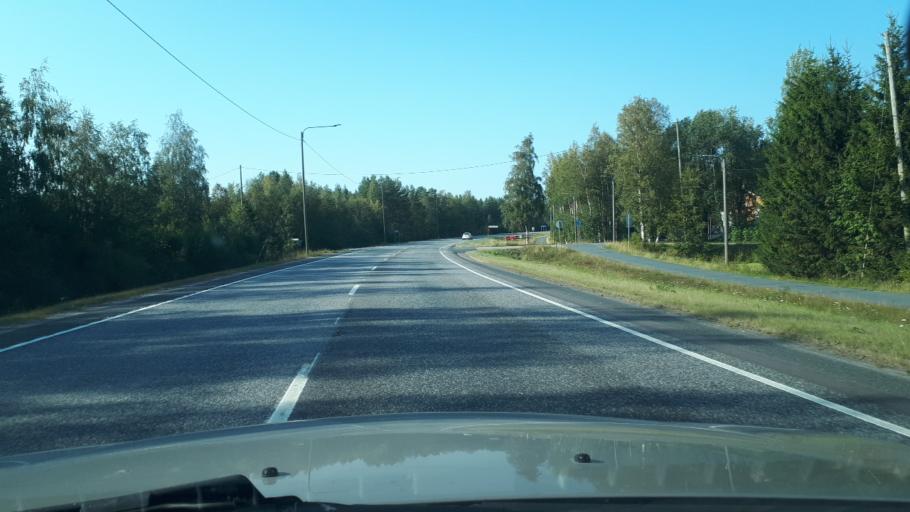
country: FI
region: Northern Ostrobothnia
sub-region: Oulunkaari
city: Ii
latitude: 65.3355
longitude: 25.3710
